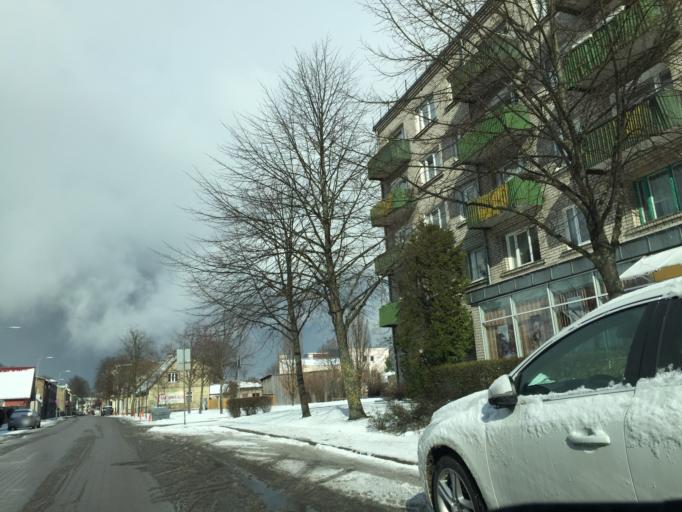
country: LV
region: Ventspils
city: Ventspils
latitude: 57.3903
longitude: 21.5592
